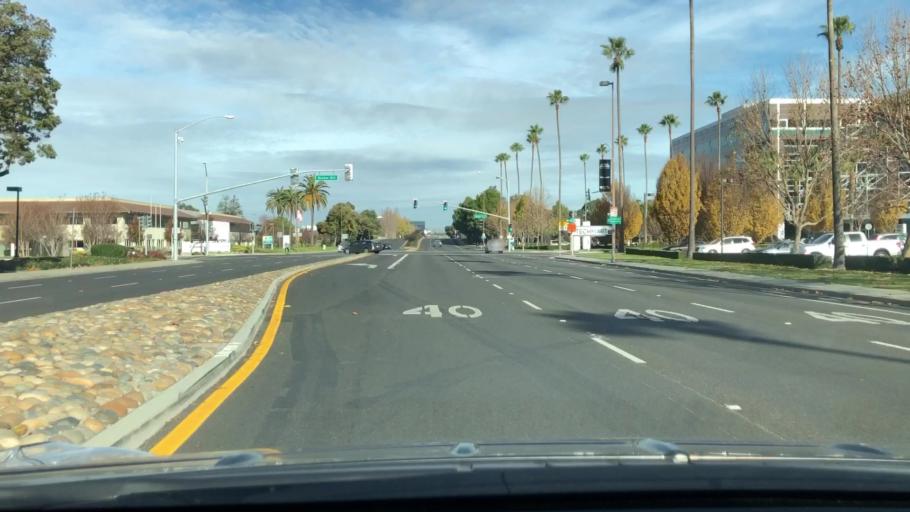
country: US
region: California
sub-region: Santa Clara County
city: Santa Clara
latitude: 37.4048
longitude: -121.9777
